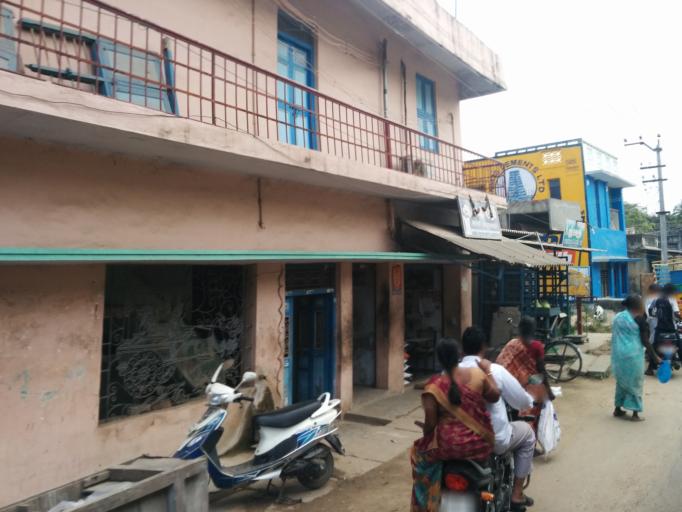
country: IN
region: Tamil Nadu
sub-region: Kancheepuram
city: Madurantakam
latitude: 12.5095
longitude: 79.8895
